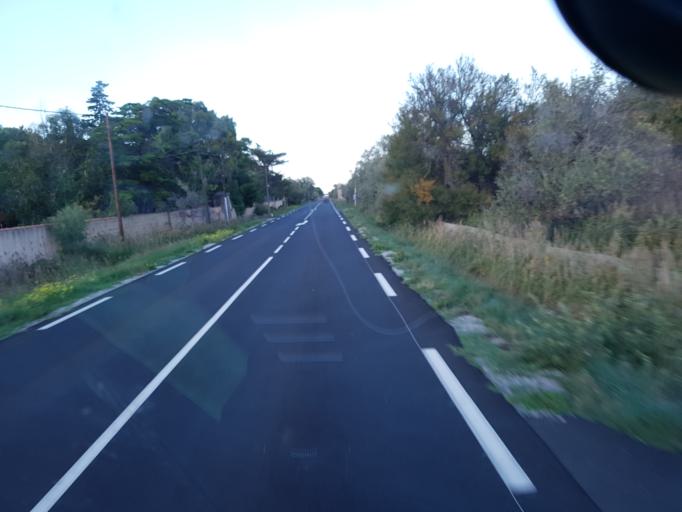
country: FR
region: Languedoc-Roussillon
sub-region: Departement de l'Aude
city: Port-la-Nouvelle
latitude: 42.9878
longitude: 3.0346
